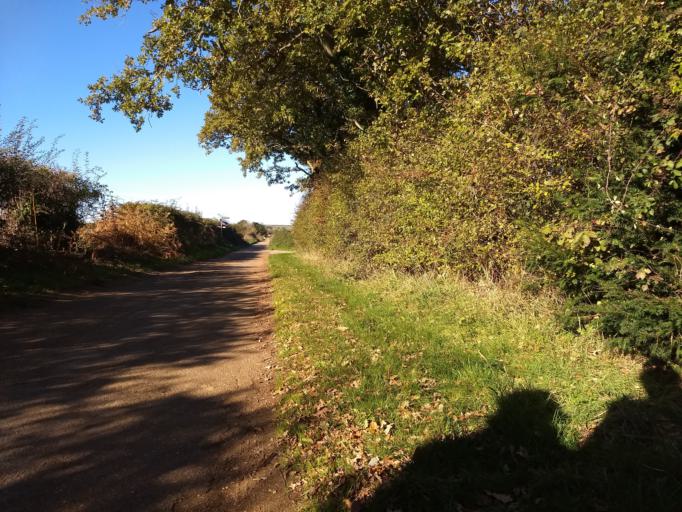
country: GB
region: England
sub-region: Isle of Wight
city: Newport
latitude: 50.6682
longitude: -1.2807
